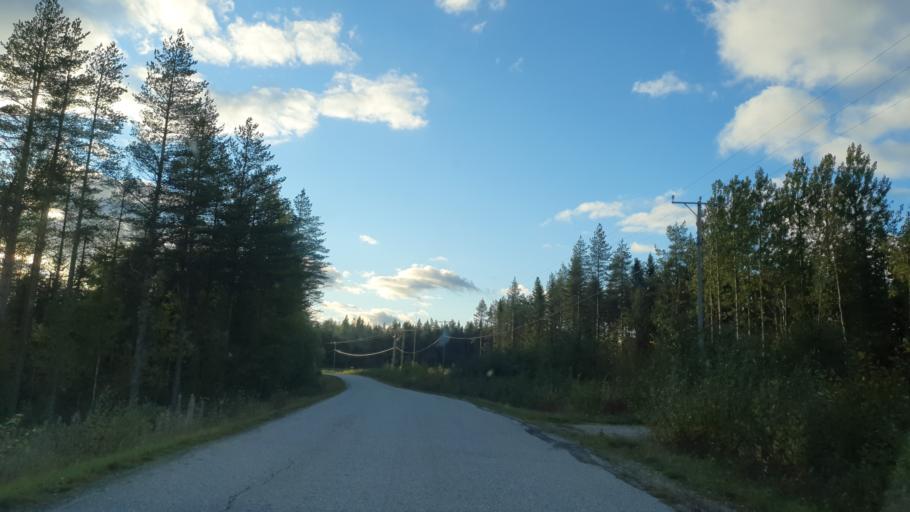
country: FI
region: Kainuu
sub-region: Kehys-Kainuu
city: Kuhmo
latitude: 63.9545
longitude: 29.7349
